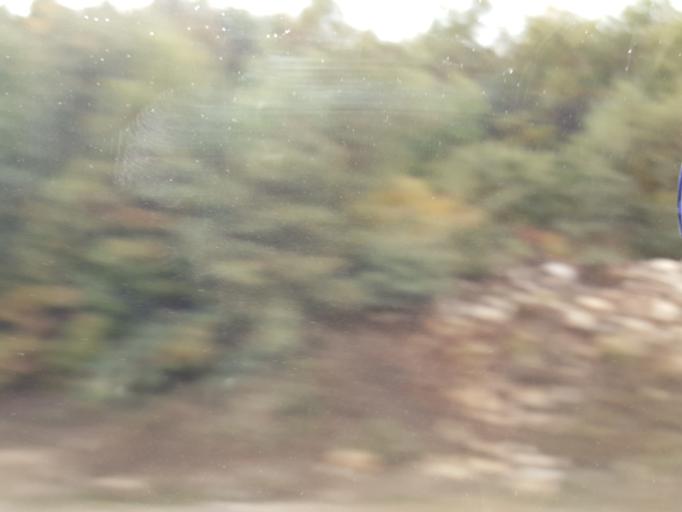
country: TR
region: Amasya
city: Gediksaray
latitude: 40.4440
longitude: 35.7790
